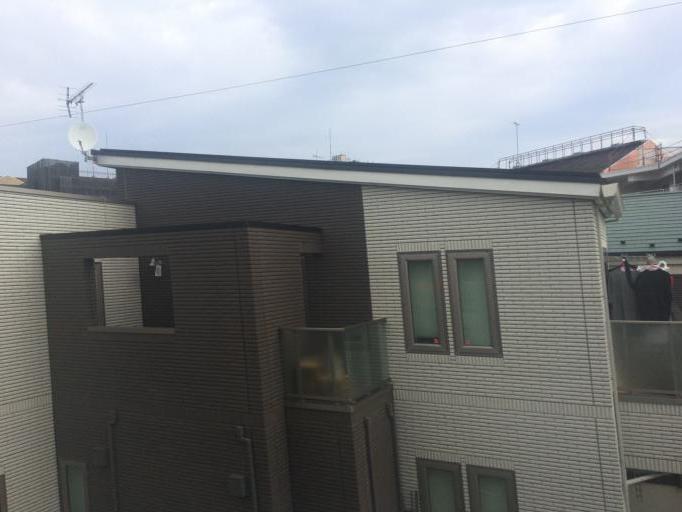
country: JP
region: Tokyo
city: Fussa
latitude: 35.7138
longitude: 139.3534
